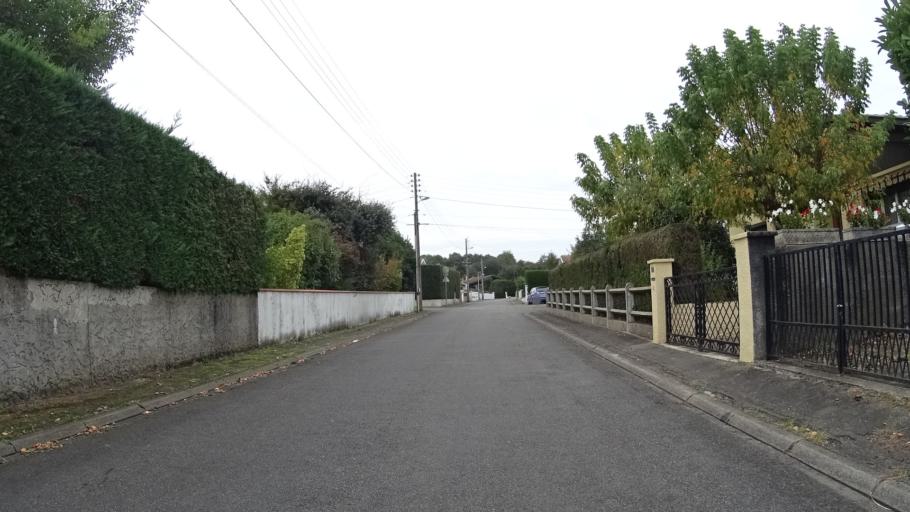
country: FR
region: Aquitaine
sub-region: Departement des Landes
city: Saint-Paul-les-Dax
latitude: 43.7305
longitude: -1.0767
